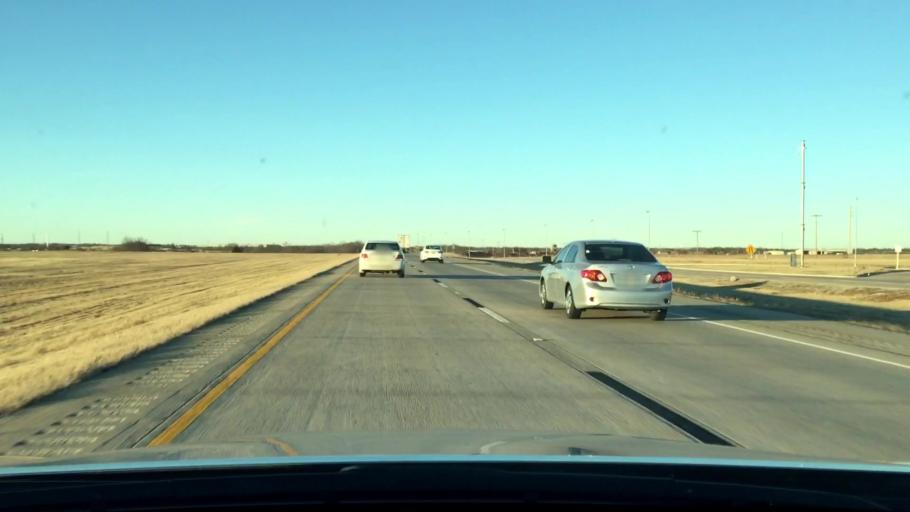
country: US
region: Oklahoma
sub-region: Love County
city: Marietta
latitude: 33.9053
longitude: -97.1342
